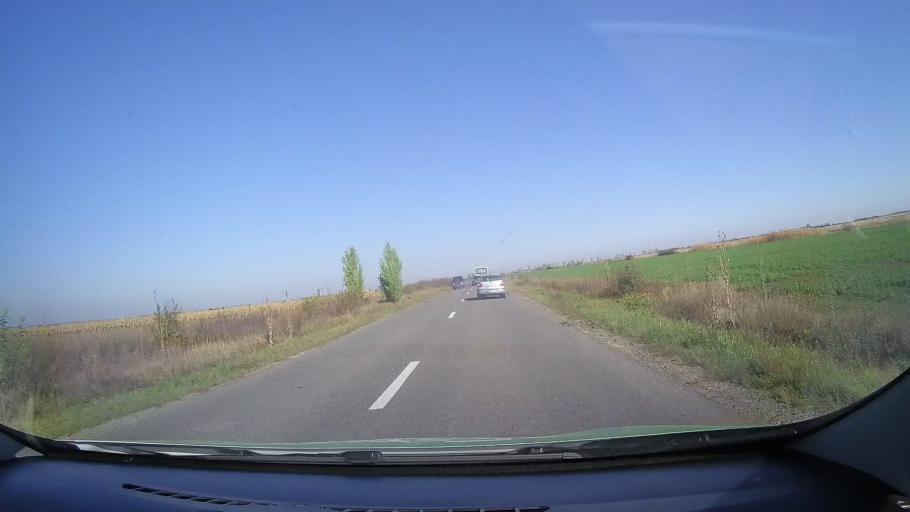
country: RO
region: Satu Mare
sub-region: Comuna Cauas
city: Cauas
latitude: 47.5834
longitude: 22.5475
